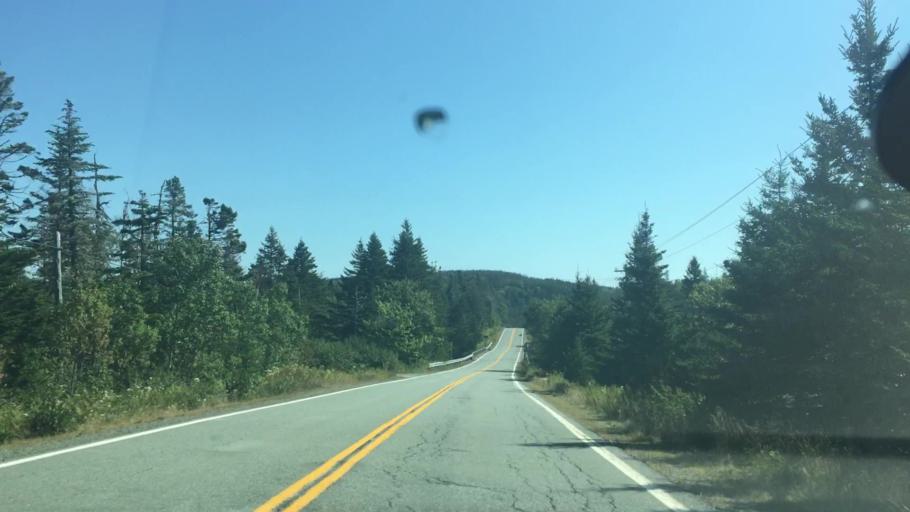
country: CA
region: Nova Scotia
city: Antigonish
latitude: 45.0132
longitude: -62.0990
